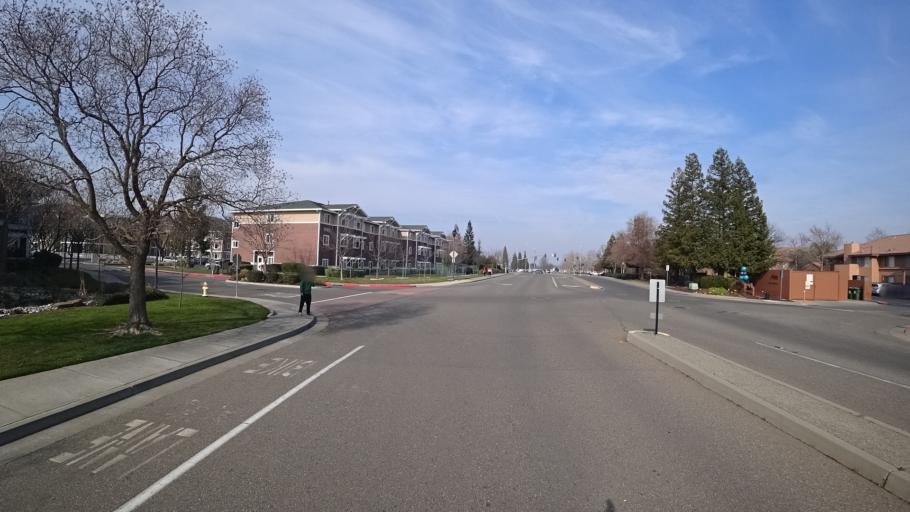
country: US
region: California
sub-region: Yolo County
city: Davis
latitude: 38.5596
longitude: -121.7727
